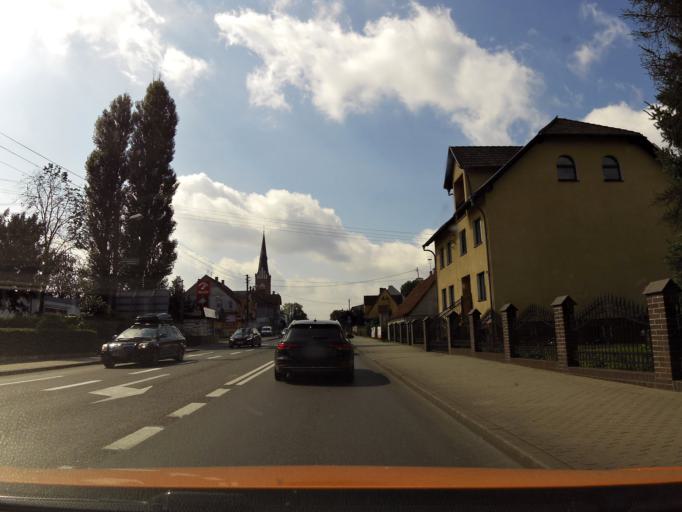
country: PL
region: West Pomeranian Voivodeship
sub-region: Powiat gryficki
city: Ploty
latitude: 53.8053
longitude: 15.2708
